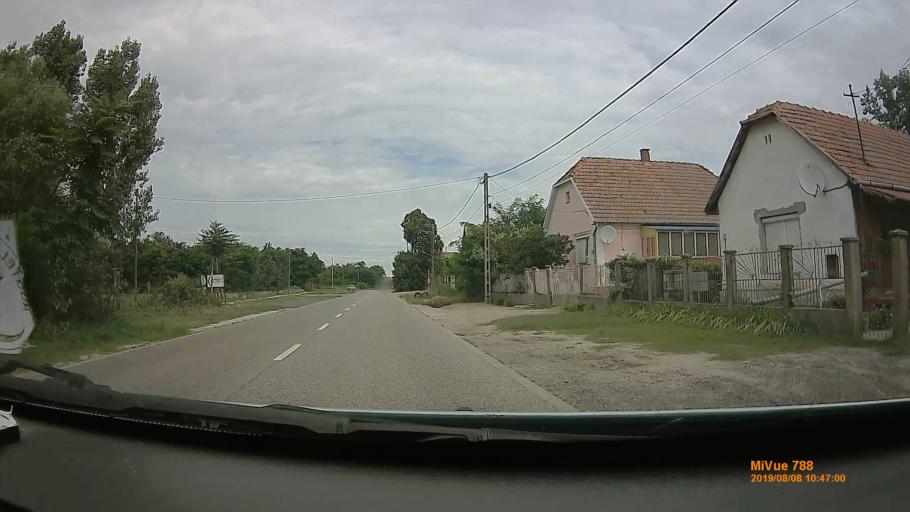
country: HU
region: Szabolcs-Szatmar-Bereg
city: Balkany
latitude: 47.7580
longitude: 21.8624
